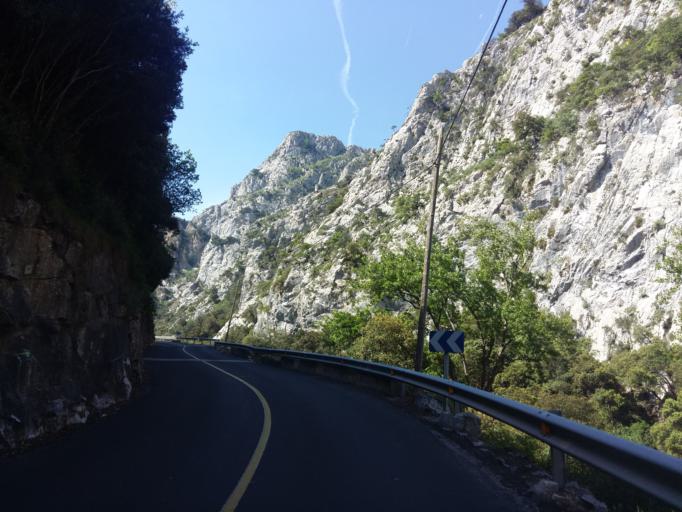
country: ES
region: Cantabria
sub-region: Provincia de Cantabria
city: Potes
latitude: 43.2114
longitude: -4.5950
